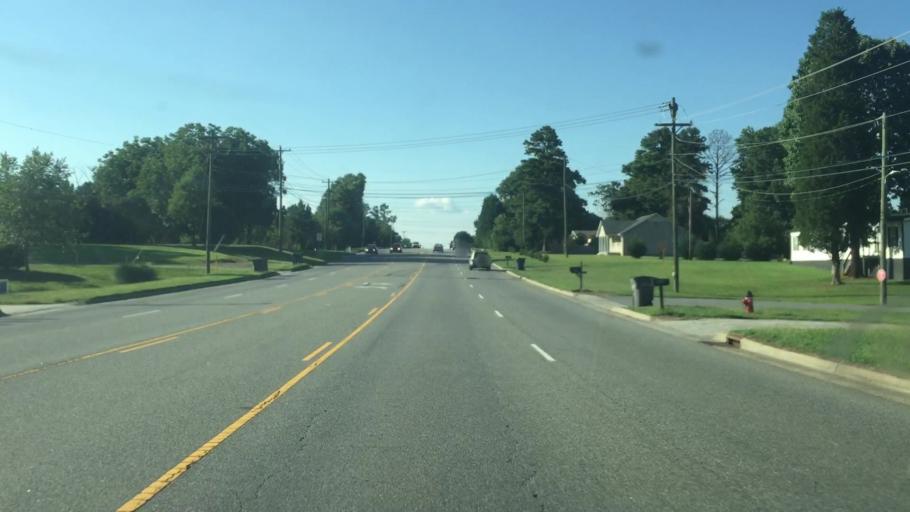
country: US
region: North Carolina
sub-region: Cabarrus County
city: Kannapolis
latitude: 35.4267
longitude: -80.6789
